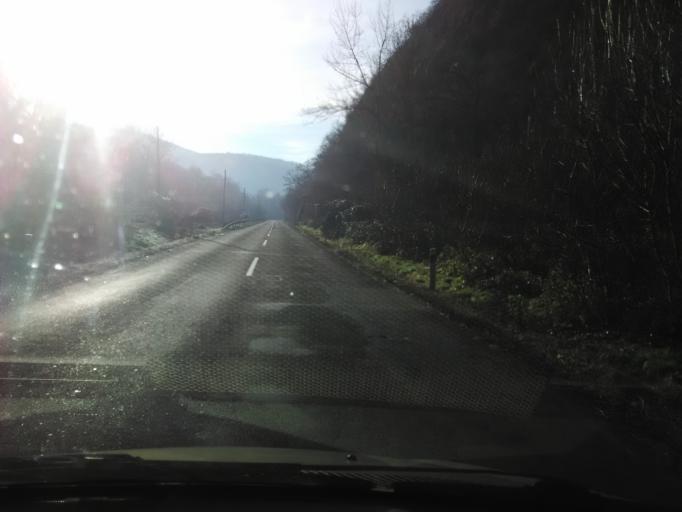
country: SK
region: Nitriansky
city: Tlmace
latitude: 48.3404
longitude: 18.5576
